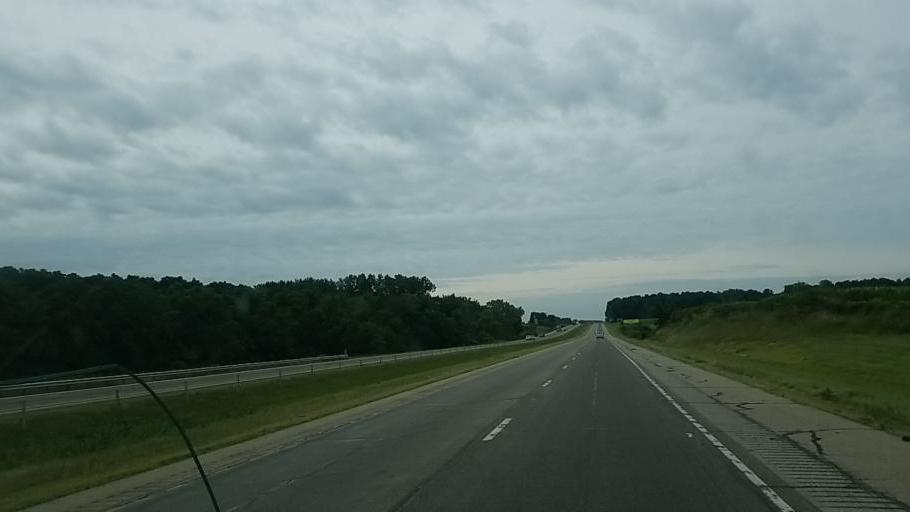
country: US
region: Indiana
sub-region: Steuben County
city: Angola
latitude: 41.5561
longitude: -85.0572
